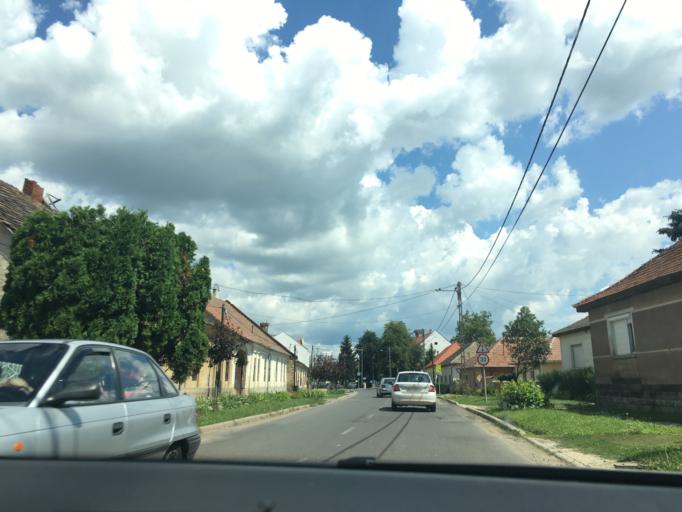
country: HU
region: Borsod-Abauj-Zemplen
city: Tarcal
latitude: 48.1615
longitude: 21.3642
